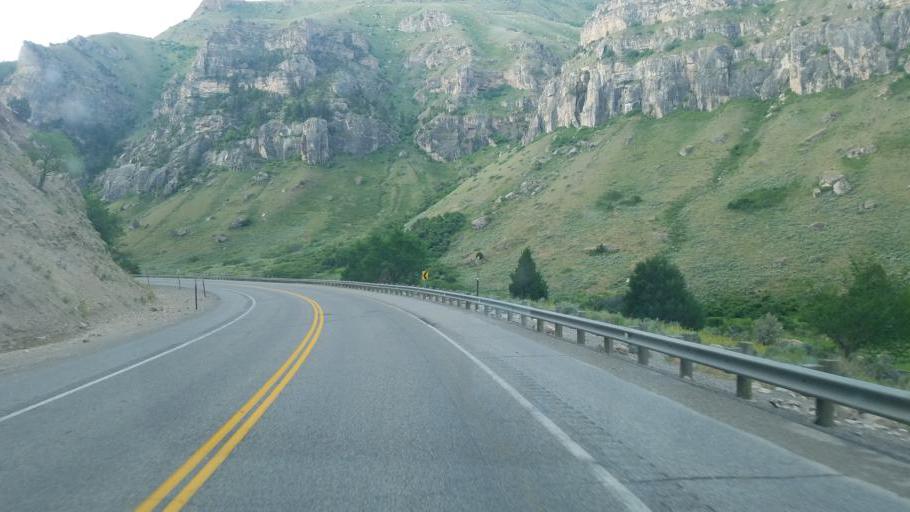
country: US
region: Wyoming
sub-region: Hot Springs County
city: Thermopolis
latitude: 43.5141
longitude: -108.1853
